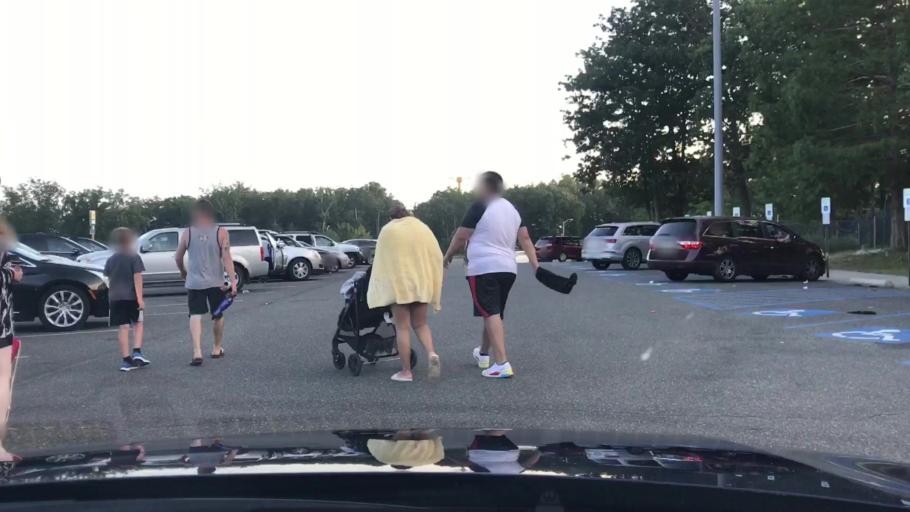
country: US
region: New Jersey
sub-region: Monmouth County
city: Shrewsbury
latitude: 40.1460
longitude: -74.4366
